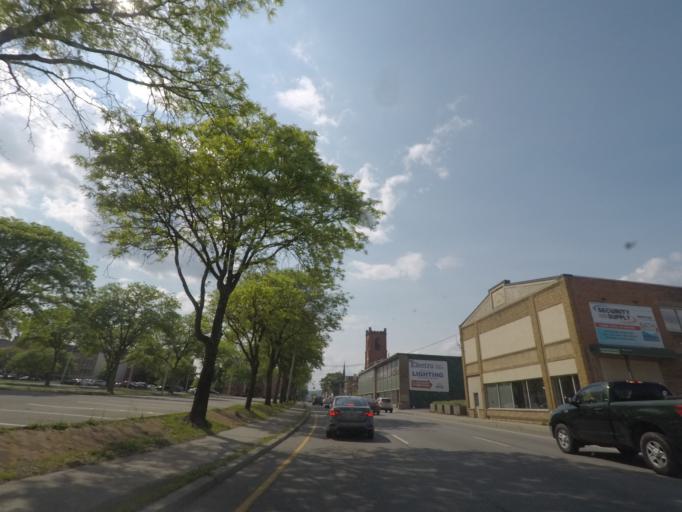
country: US
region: New York
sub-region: Dutchess County
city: Poughkeepsie
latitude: 41.7036
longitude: -73.9230
